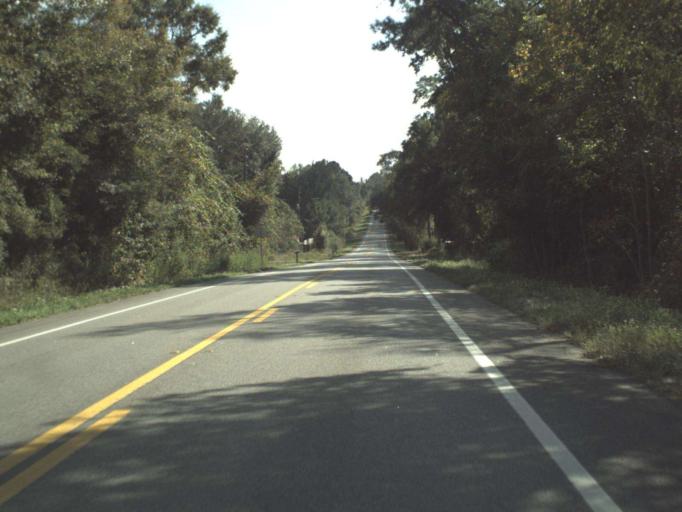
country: US
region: Florida
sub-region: Jefferson County
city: Monticello
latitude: 30.5082
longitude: -84.0243
